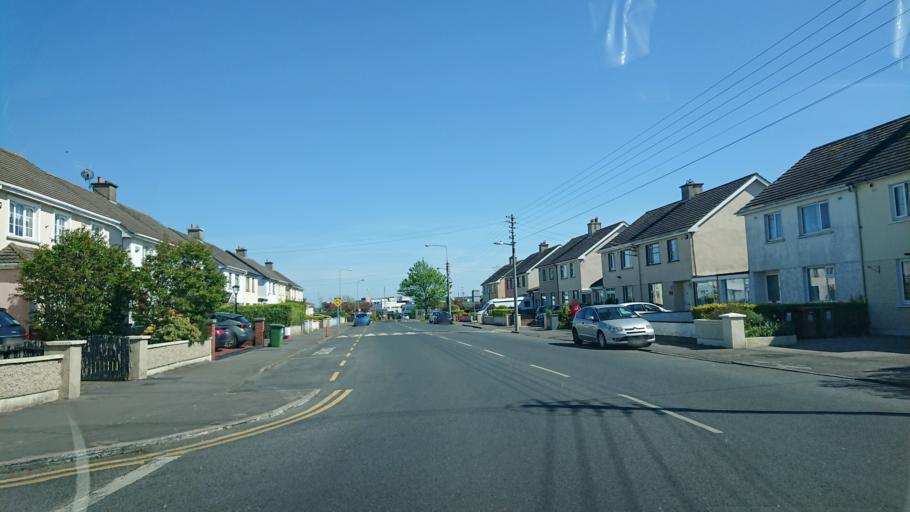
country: IE
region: Munster
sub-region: Waterford
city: Waterford
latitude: 52.2483
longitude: -7.1431
